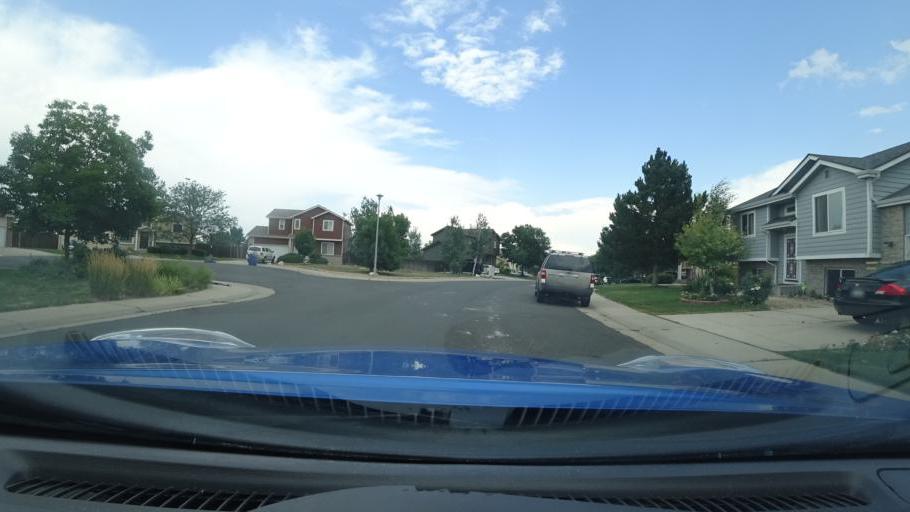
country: US
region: Colorado
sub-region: Adams County
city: Aurora
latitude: 39.6900
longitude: -104.7895
